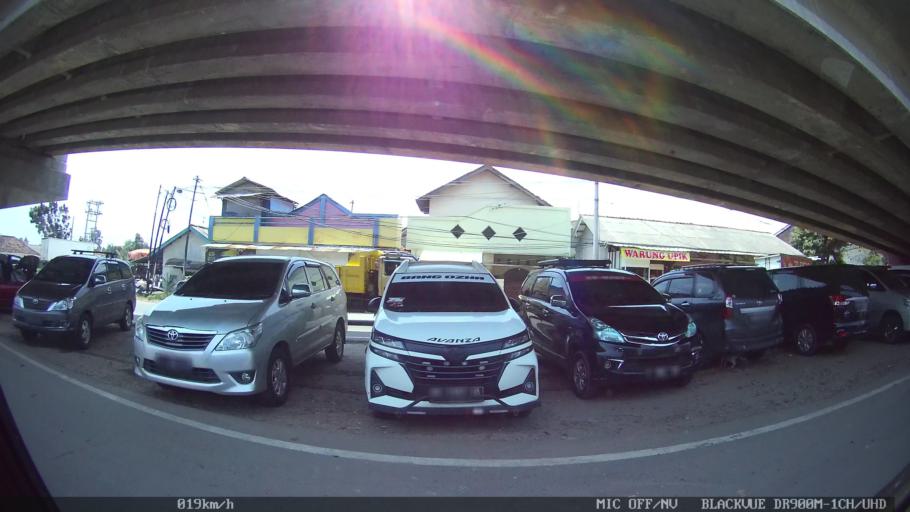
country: ID
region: Lampung
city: Kedaton
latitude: -5.3615
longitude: 105.2566
